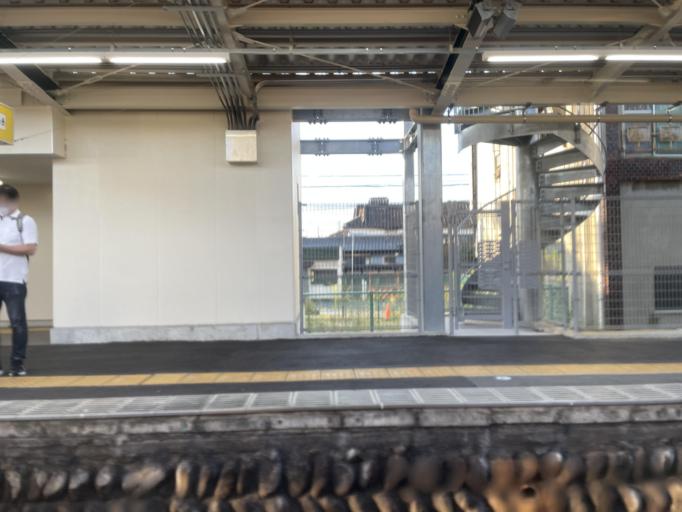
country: JP
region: Osaka
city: Matsubara
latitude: 34.5752
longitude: 135.5462
